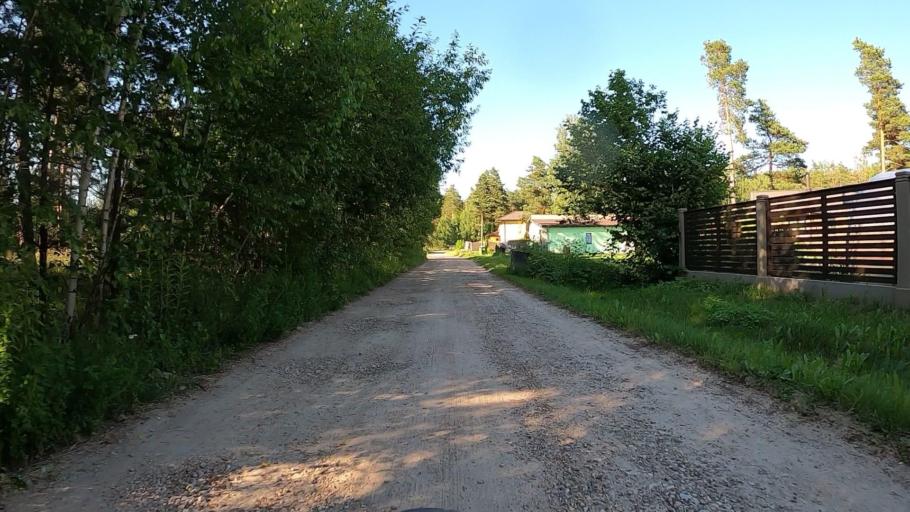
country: LV
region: Stopini
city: Ulbroka
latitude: 56.8789
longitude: 24.2977
